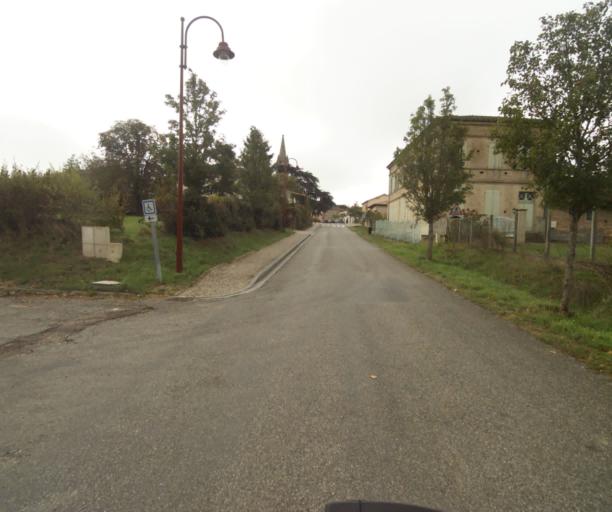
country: FR
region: Midi-Pyrenees
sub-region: Departement du Tarn-et-Garonne
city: Campsas
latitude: 43.8984
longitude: 1.3260
